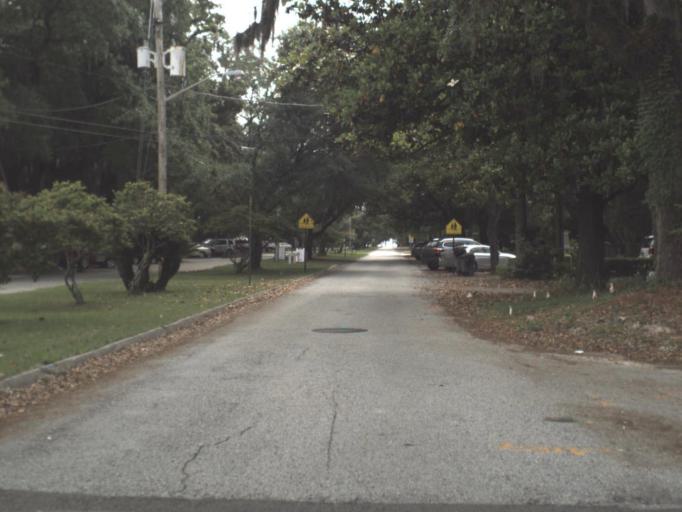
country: US
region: Florida
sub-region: Clay County
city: Orange Park
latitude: 30.1659
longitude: -81.7009
